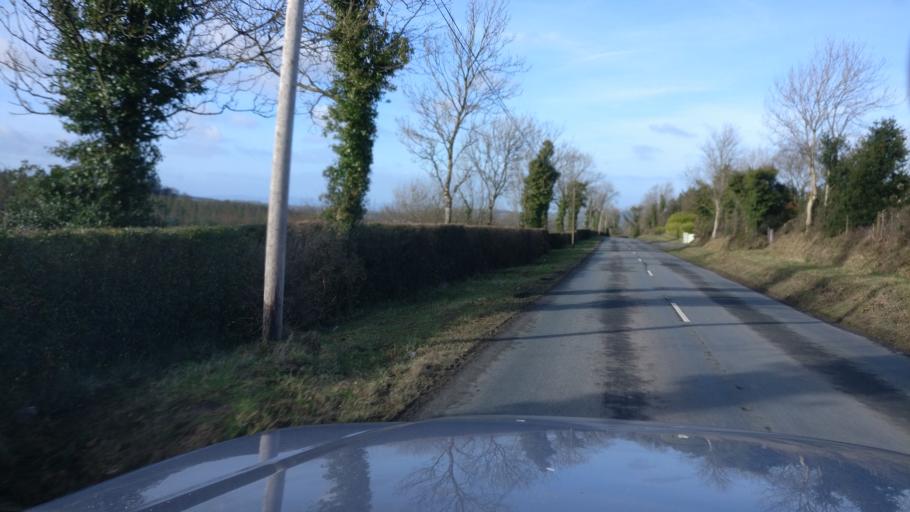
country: IE
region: Leinster
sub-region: Laois
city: Stradbally
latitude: 52.9373
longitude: -7.1969
